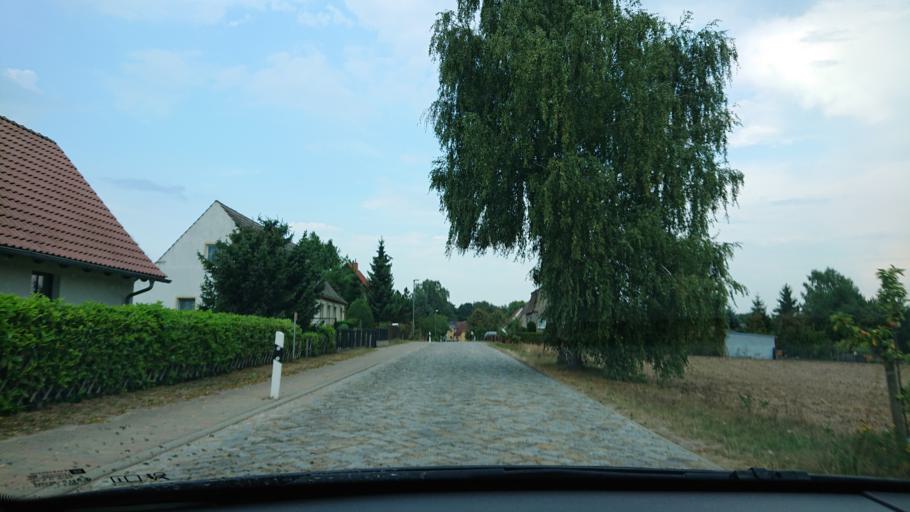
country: DE
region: Mecklenburg-Vorpommern
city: Kemnitz
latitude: 54.0388
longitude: 13.5379
